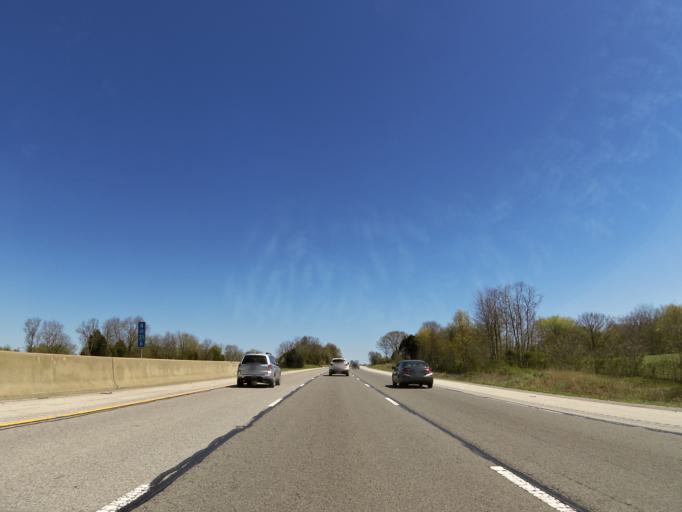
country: US
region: Kentucky
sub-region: Warren County
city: Bowling Green
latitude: 37.0125
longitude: -86.3055
